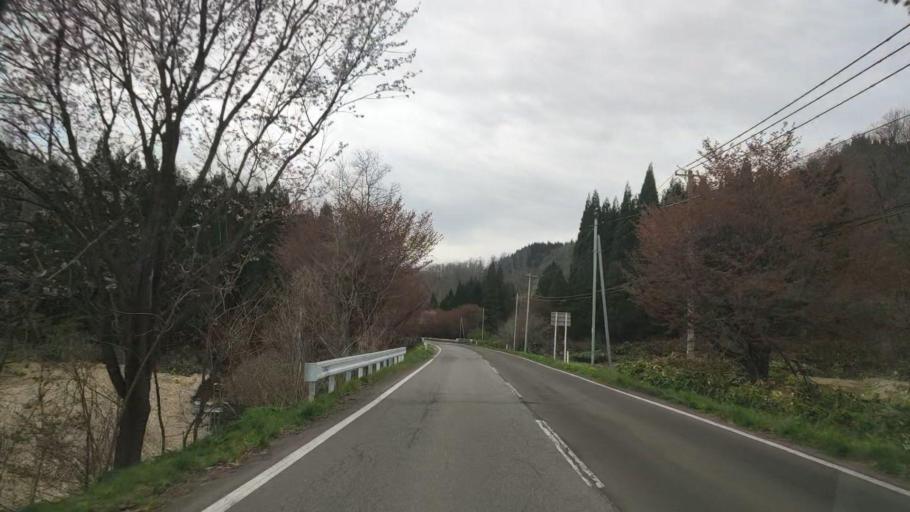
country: JP
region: Akita
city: Hanawa
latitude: 40.3533
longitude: 140.7785
